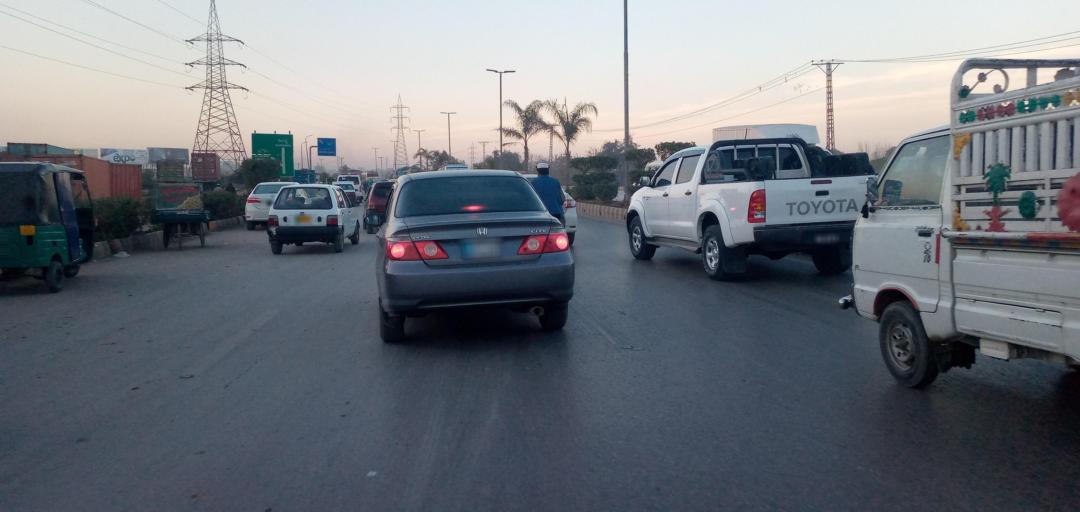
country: PK
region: Khyber Pakhtunkhwa
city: Peshawar
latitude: 34.0245
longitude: 71.6201
